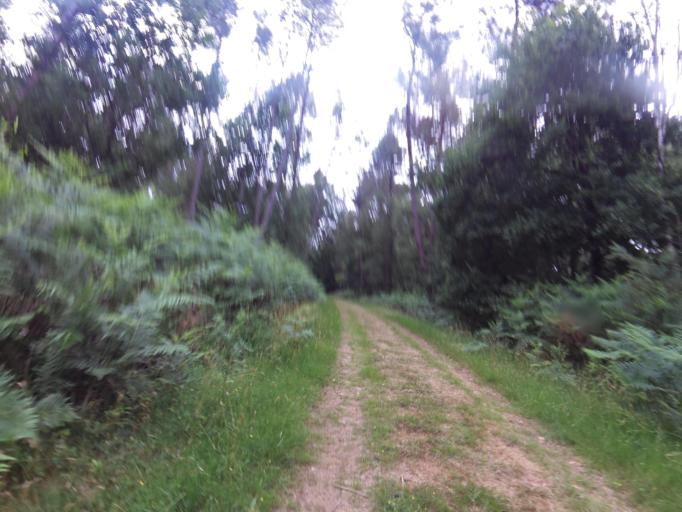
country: FR
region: Brittany
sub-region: Departement du Morbihan
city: Molac
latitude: 47.7598
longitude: -2.4158
